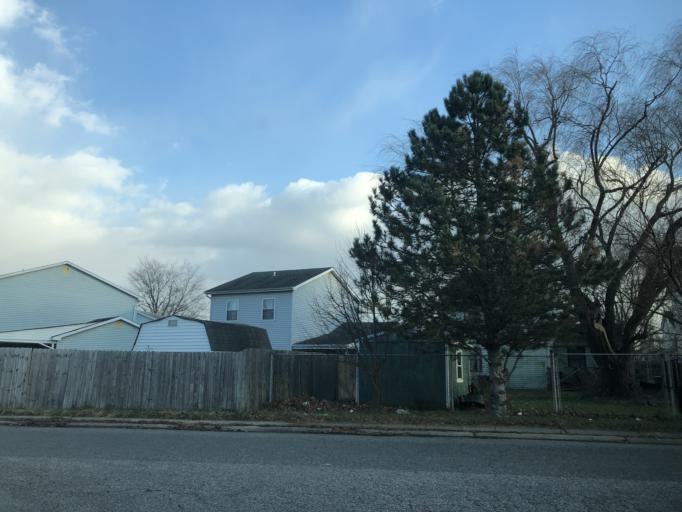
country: US
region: Delaware
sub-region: New Castle County
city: Bear
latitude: 39.6390
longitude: -75.6475
